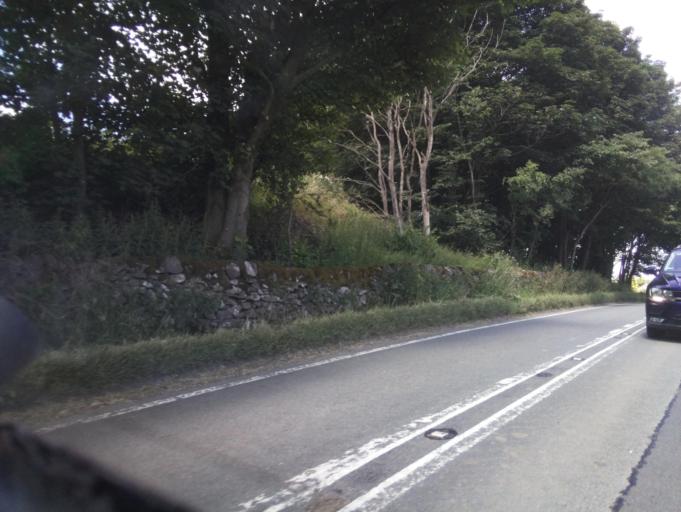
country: GB
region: England
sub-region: Derbyshire
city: Ashbourne
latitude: 53.0973
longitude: -1.7728
